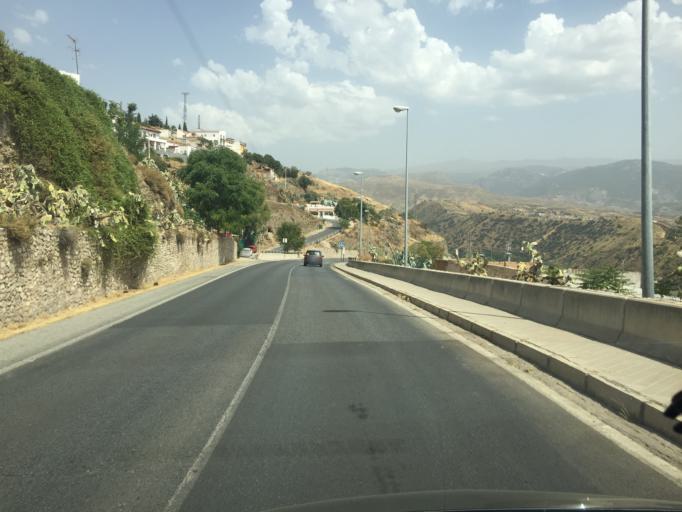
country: ES
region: Andalusia
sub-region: Provincia de Granada
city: Huetor Vega
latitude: 37.1690
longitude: -3.5841
